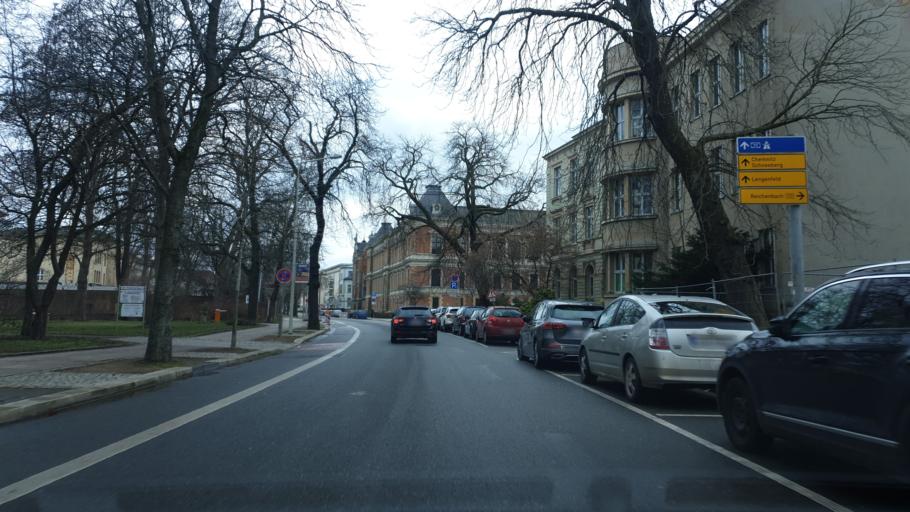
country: DE
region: Saxony
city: Zwickau
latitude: 50.7177
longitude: 12.4922
